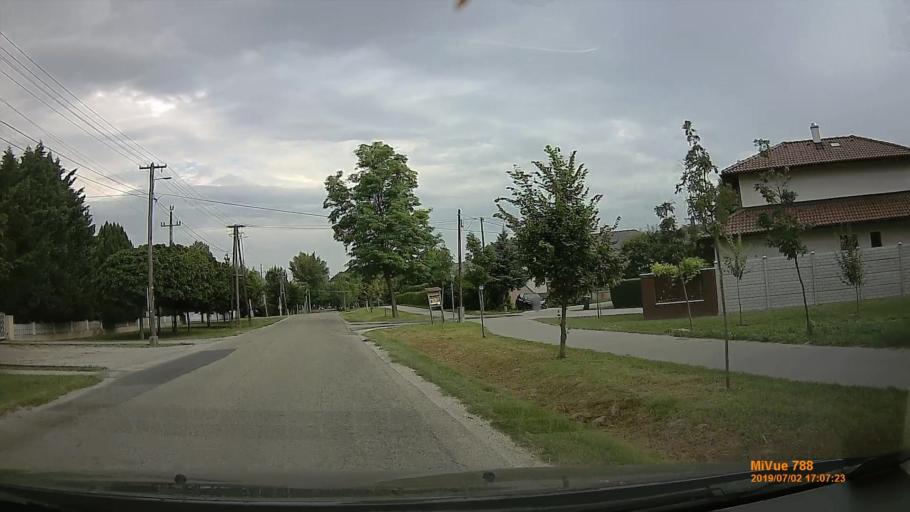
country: HU
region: Gyor-Moson-Sopron
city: Mosonmagyarovar
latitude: 47.8743
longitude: 17.2857
